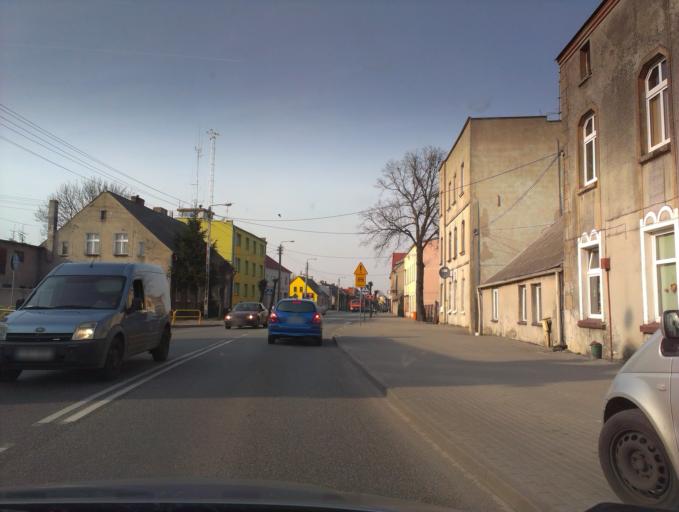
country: PL
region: Kujawsko-Pomorskie
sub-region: Powiat sepolenski
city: Sepolno Krajenskie
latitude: 53.4468
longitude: 17.5287
